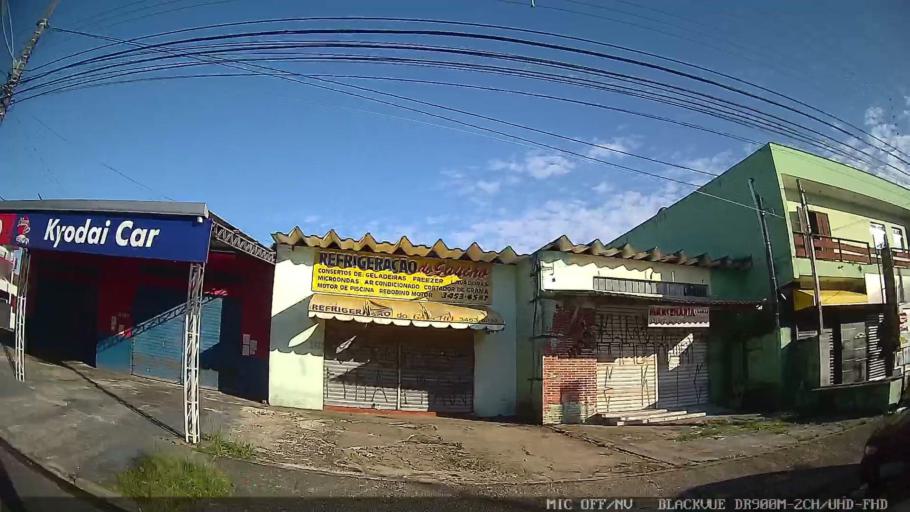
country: BR
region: Sao Paulo
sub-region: Peruibe
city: Peruibe
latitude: -24.3008
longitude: -46.9740
